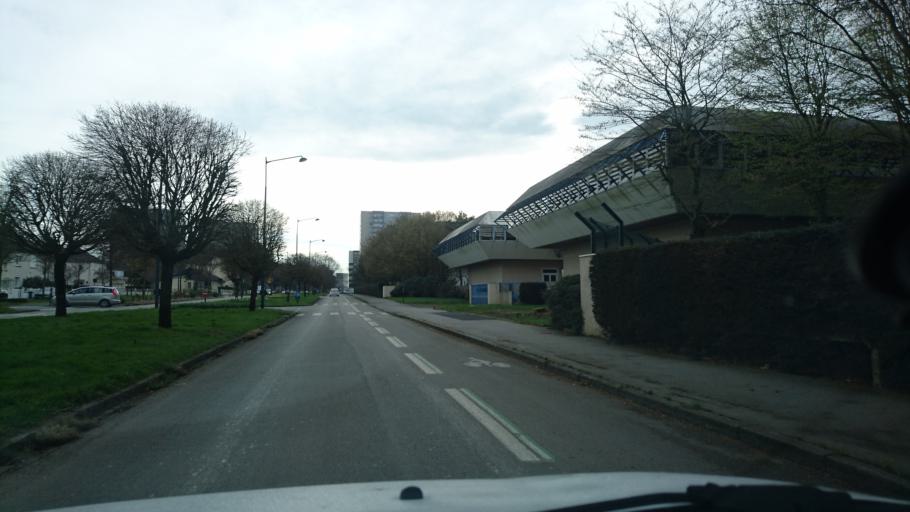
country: FR
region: Brittany
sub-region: Departement d'Ille-et-Vilaine
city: Rennes
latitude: 48.0883
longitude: -1.6667
